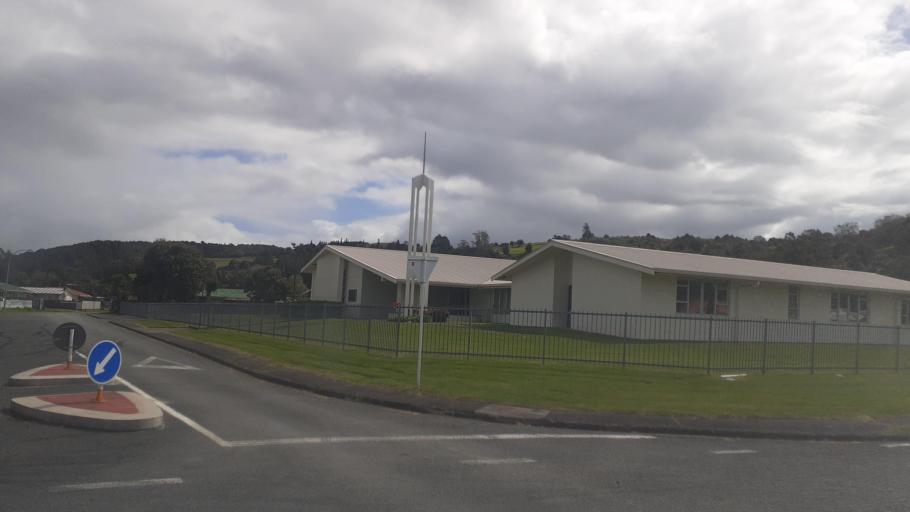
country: NZ
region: Northland
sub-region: Far North District
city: Moerewa
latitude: -35.3879
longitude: 174.0106
